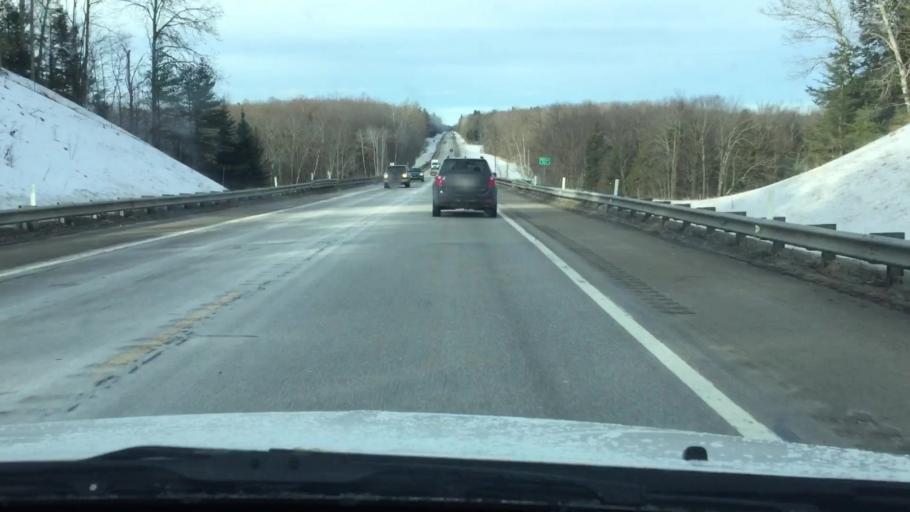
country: US
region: Michigan
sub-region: Wexford County
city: Manton
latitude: 44.4833
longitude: -85.4064
